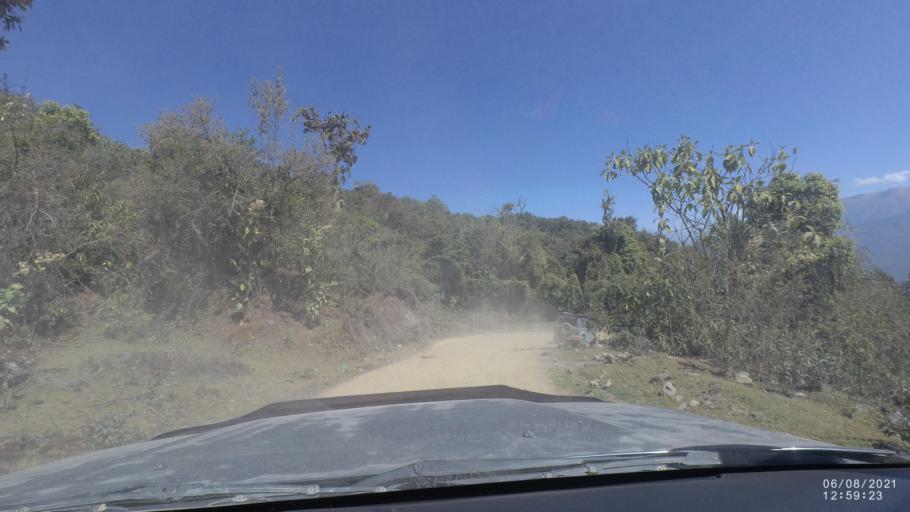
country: BO
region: Cochabamba
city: Colchani
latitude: -16.7502
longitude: -66.6868
